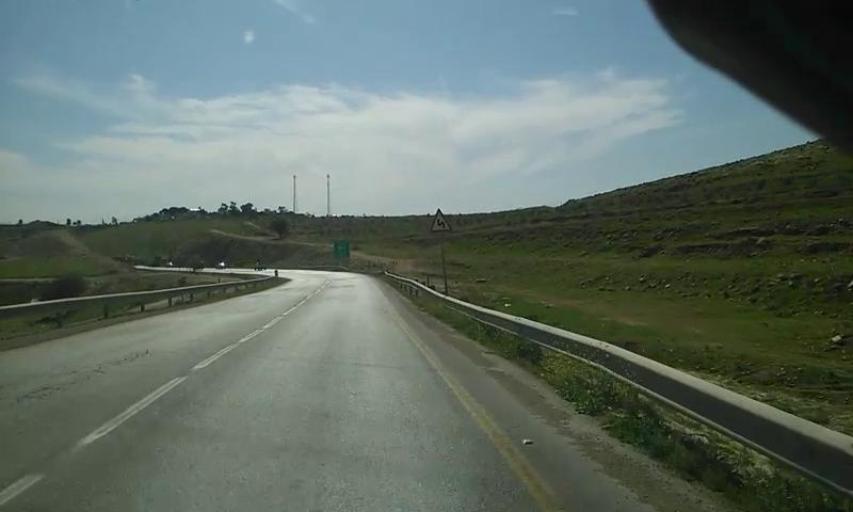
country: PS
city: Az Za`ayyim
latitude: 31.8079
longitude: 35.3224
